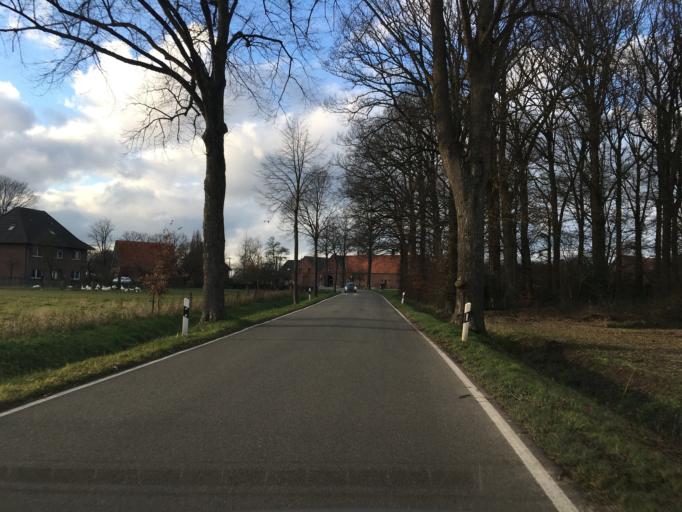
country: DE
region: North Rhine-Westphalia
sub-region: Regierungsbezirk Munster
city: Gescher
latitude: 51.9547
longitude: 7.0631
